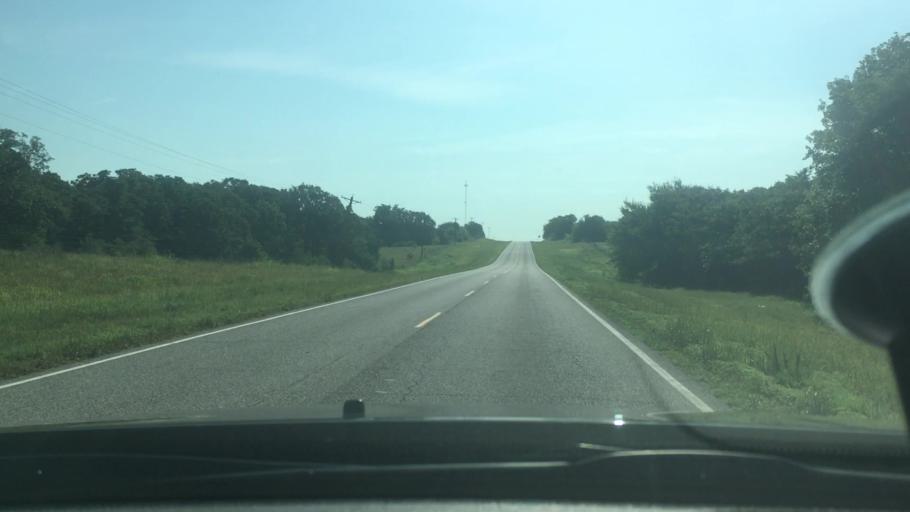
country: US
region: Oklahoma
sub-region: Garvin County
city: Pauls Valley
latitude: 34.6518
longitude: -97.2732
